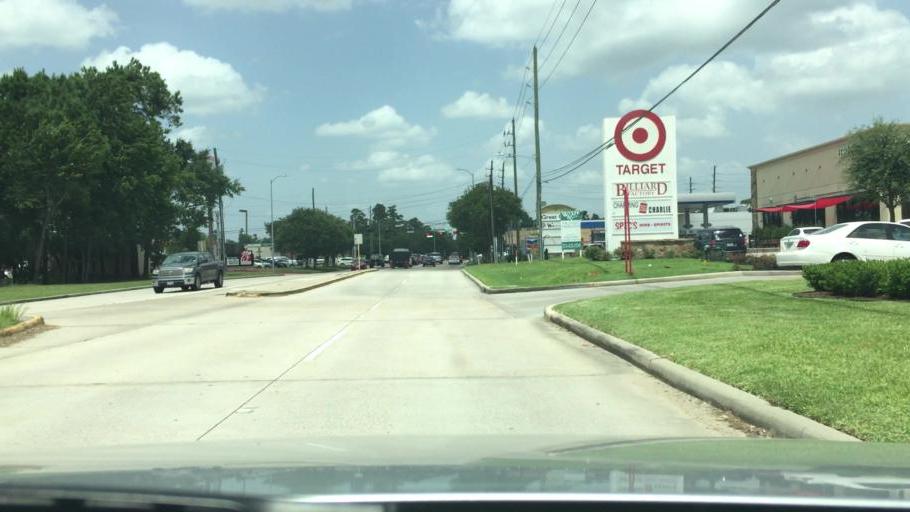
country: US
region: Texas
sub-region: Harris County
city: Hudson
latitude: 29.9672
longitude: -95.5325
